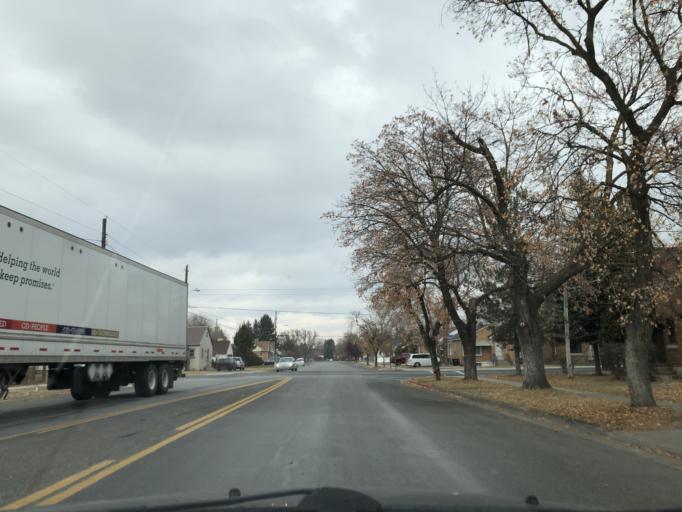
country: US
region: Utah
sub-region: Cache County
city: Logan
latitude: 41.7405
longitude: -111.8373
